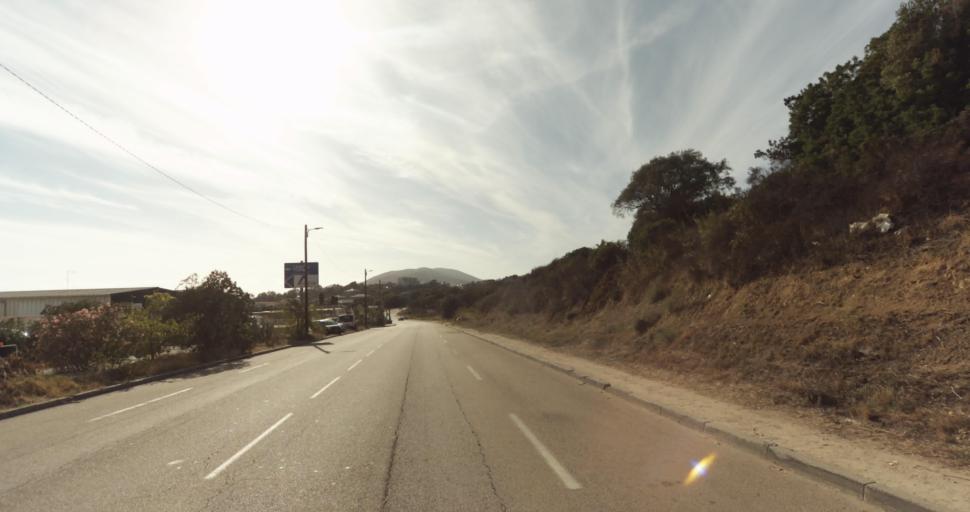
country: FR
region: Corsica
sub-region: Departement de la Corse-du-Sud
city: Ajaccio
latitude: 41.9297
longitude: 8.7739
